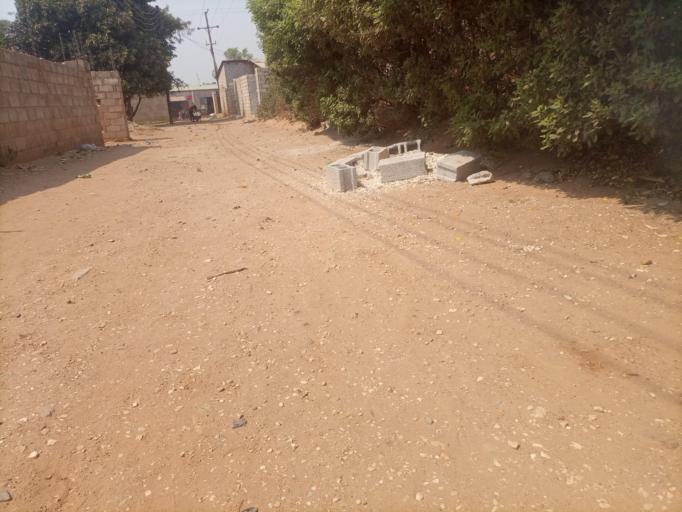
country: ZM
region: Lusaka
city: Lusaka
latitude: -15.4040
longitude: 28.3794
